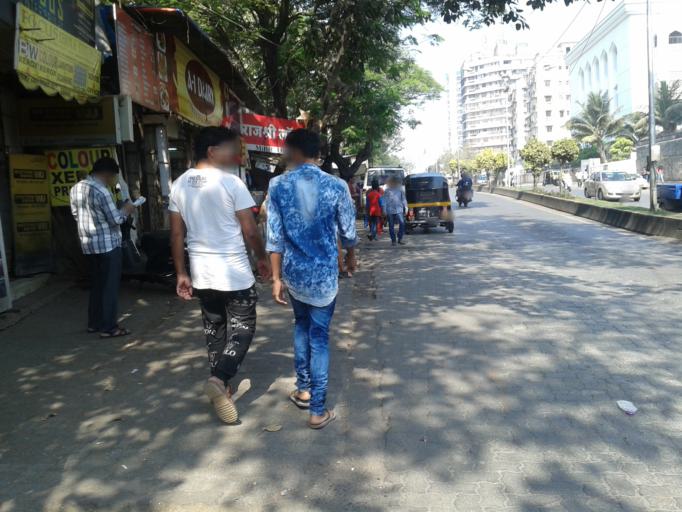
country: IN
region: Maharashtra
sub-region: Mumbai Suburban
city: Borivli
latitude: 19.2492
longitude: 72.8628
